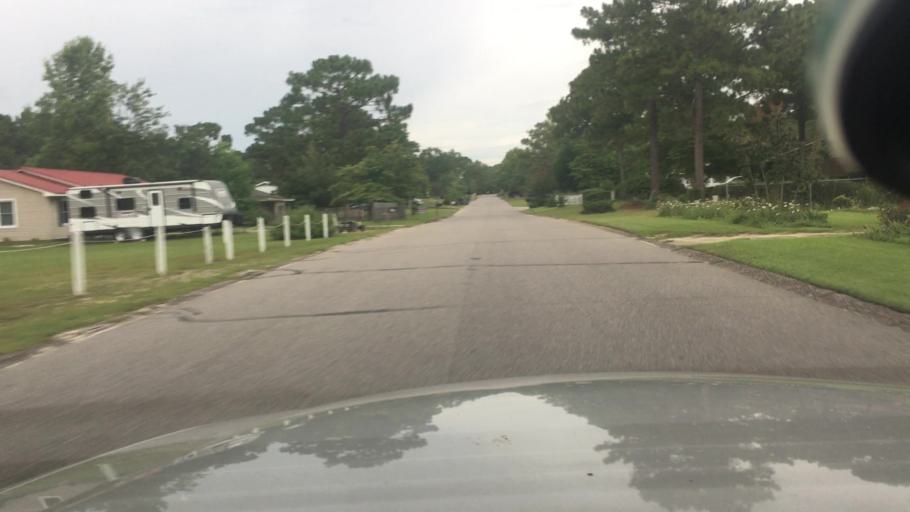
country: US
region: North Carolina
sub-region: Cumberland County
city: Hope Mills
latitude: 34.9694
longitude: -78.9755
